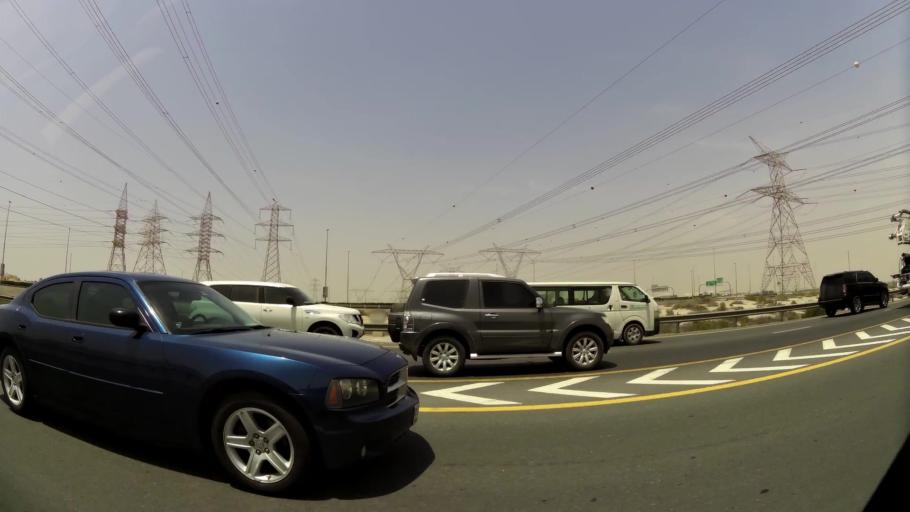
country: AE
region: Ash Shariqah
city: Sharjah
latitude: 25.2112
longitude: 55.3993
